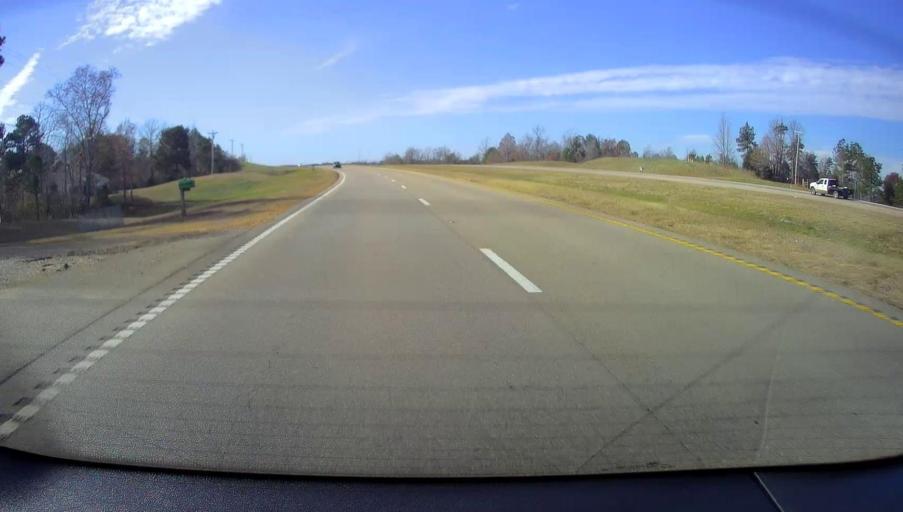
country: US
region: Mississippi
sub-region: Benton County
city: Ashland
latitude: 34.9553
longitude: -88.9882
